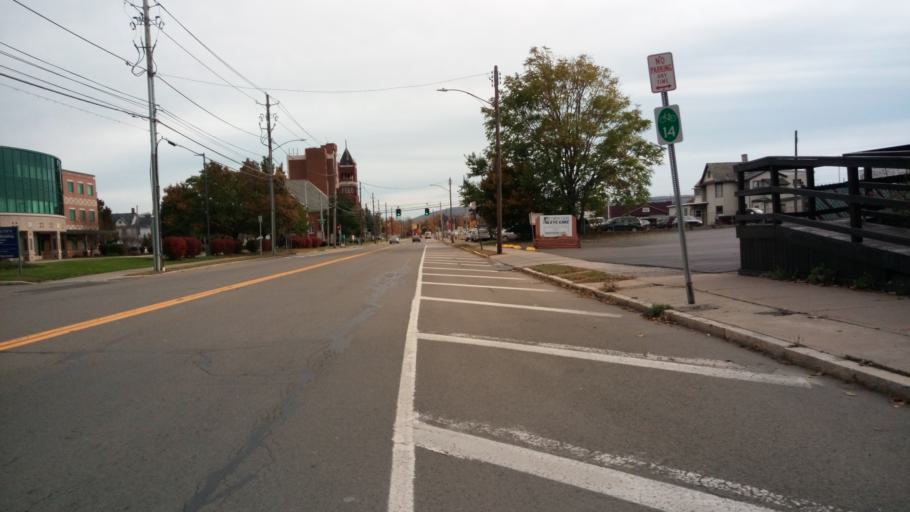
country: US
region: New York
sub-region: Chemung County
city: Elmira
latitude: 42.0917
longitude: -76.7996
